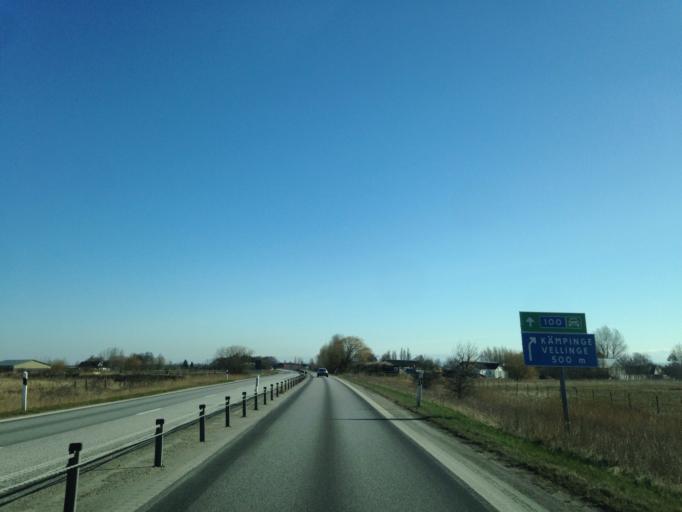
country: SE
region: Skane
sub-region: Vellinge Kommun
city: Hollviken
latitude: 55.4338
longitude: 12.9780
